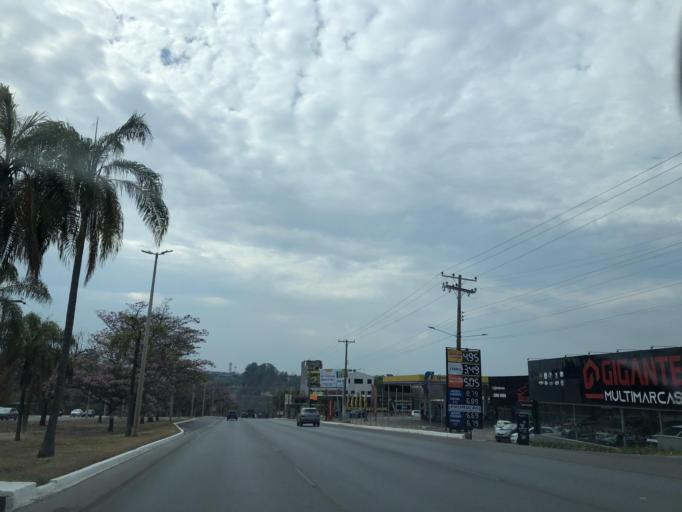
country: BR
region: Federal District
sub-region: Brasilia
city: Brasilia
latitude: -15.8500
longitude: -48.0733
